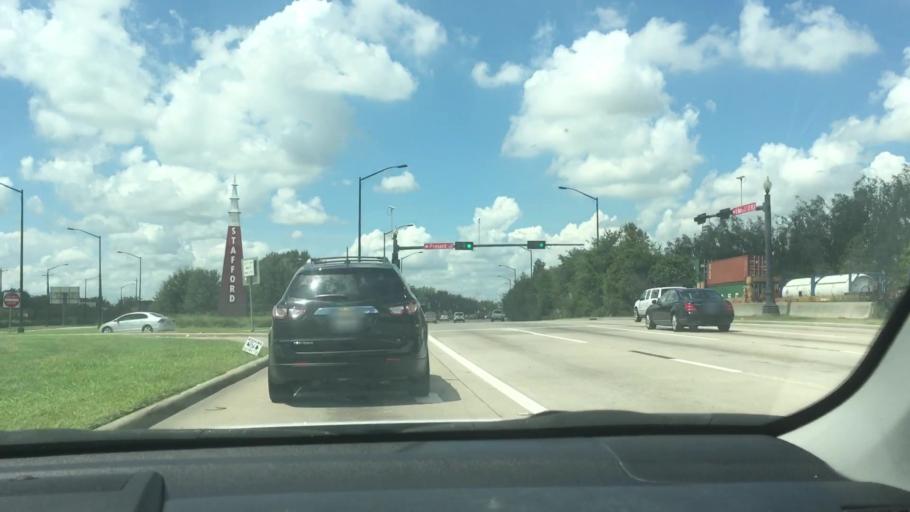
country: US
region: Texas
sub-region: Fort Bend County
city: Missouri City
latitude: 29.6160
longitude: -95.5466
